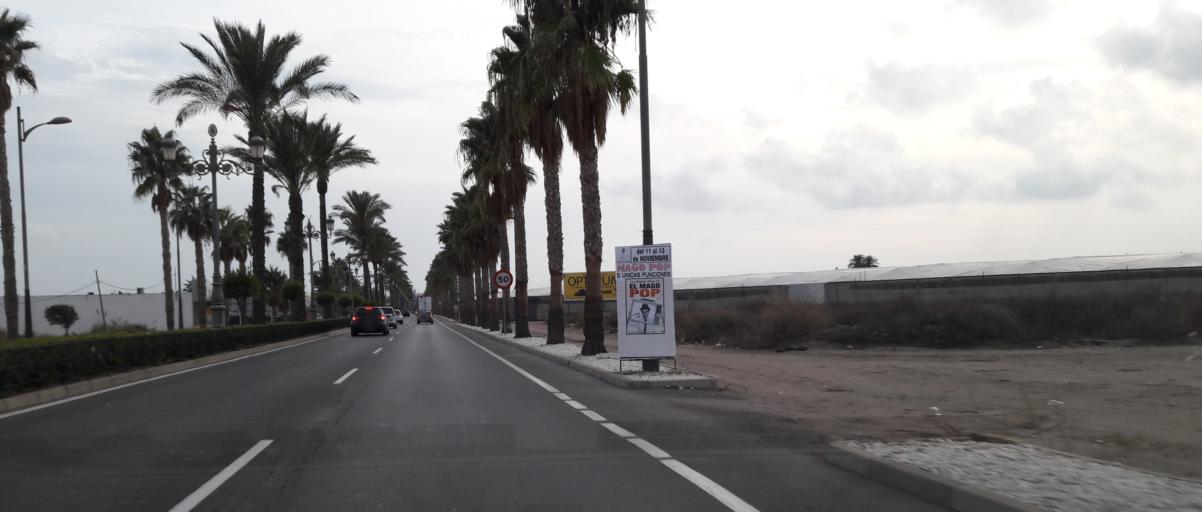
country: ES
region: Andalusia
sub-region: Provincia de Almeria
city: Aguadulce
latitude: 36.7981
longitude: -2.6021
